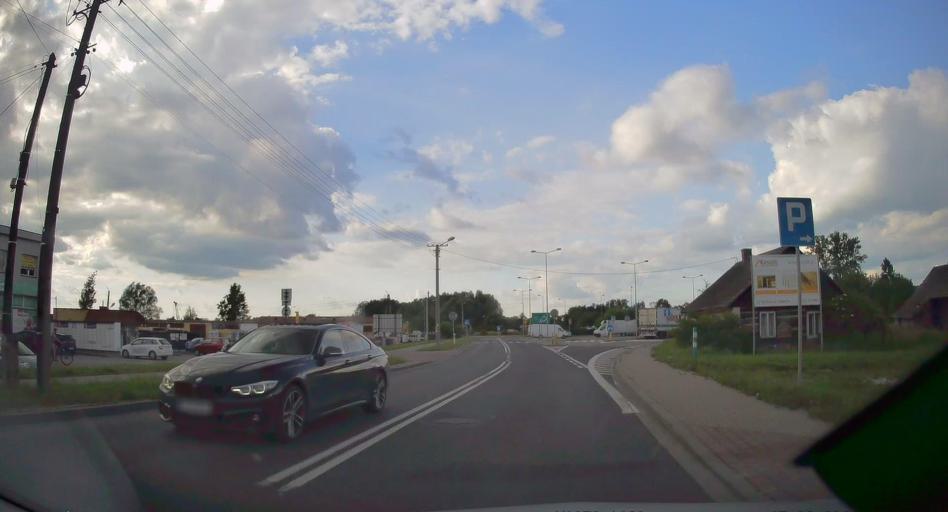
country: PL
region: Lesser Poland Voivodeship
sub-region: Powiat oswiecimski
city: Kety
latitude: 49.8890
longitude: 19.2301
